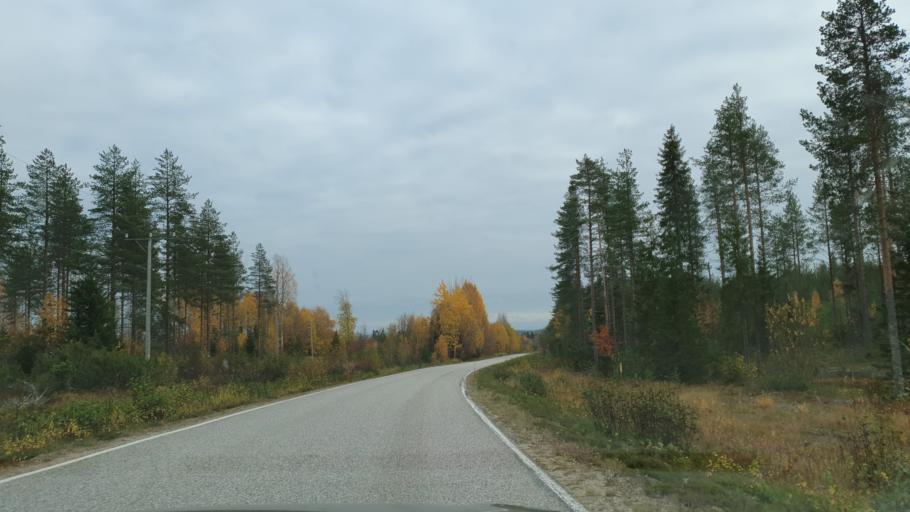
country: FI
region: Kainuu
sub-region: Kajaani
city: Ristijaervi
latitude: 64.4703
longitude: 28.2975
